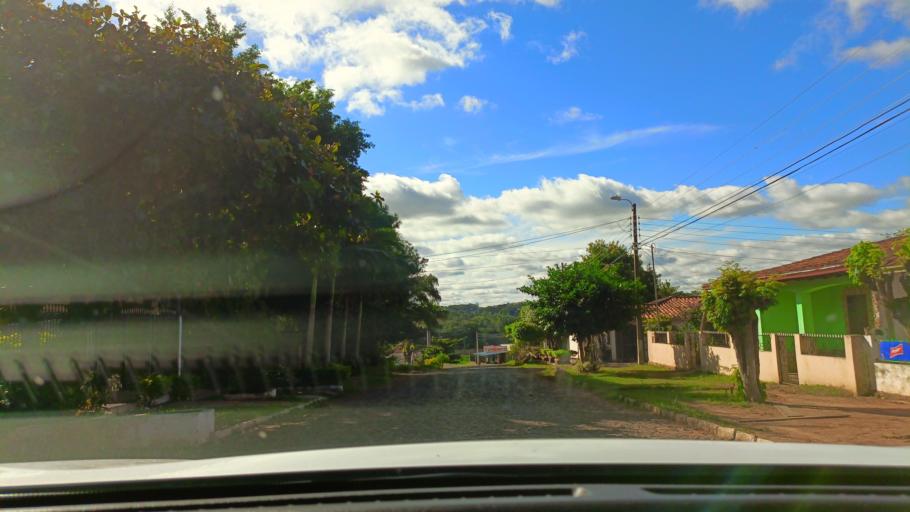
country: PY
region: San Pedro
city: Guayaybi
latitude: -24.6584
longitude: -56.4433
